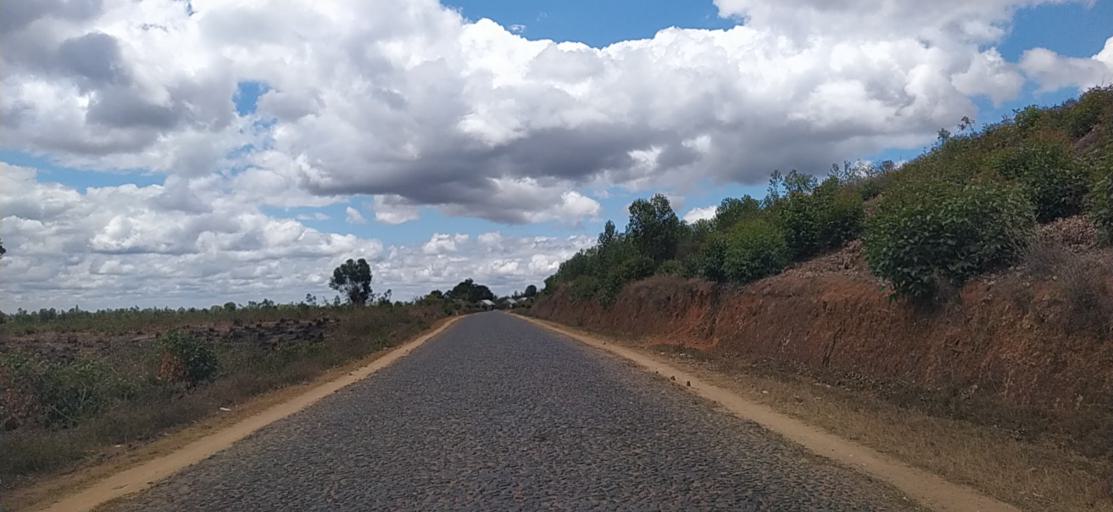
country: MG
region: Alaotra Mangoro
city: Moramanga
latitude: -18.7554
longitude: 48.2593
